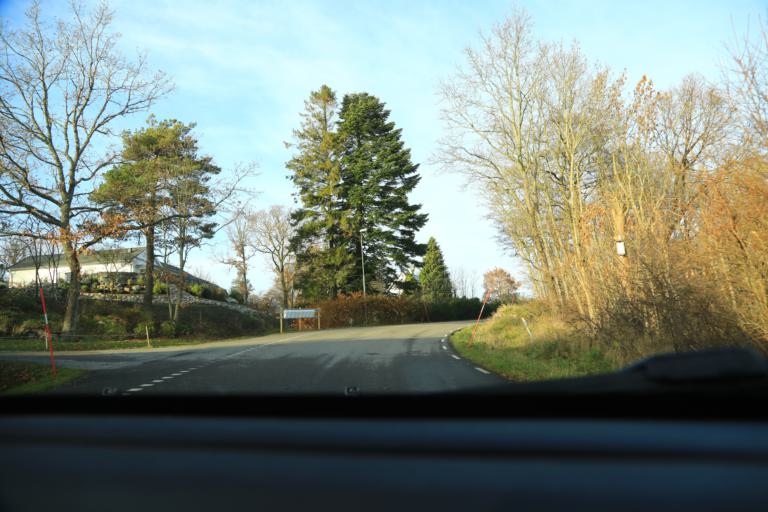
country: SE
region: Halland
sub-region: Varbergs Kommun
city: Varberg
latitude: 57.1875
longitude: 12.2195
